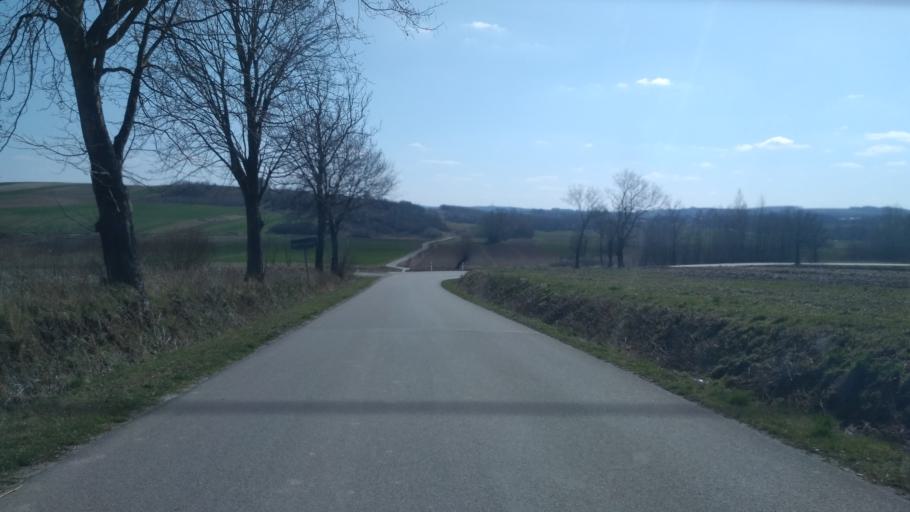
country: PL
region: Subcarpathian Voivodeship
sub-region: Powiat przeworski
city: Pantalowice
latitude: 49.9481
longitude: 22.4397
